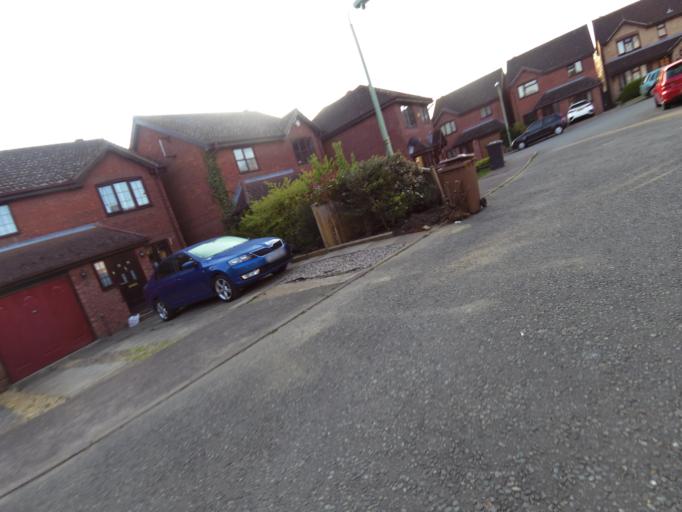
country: GB
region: England
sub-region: Suffolk
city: Bramford
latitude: 52.0370
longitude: 1.0891
